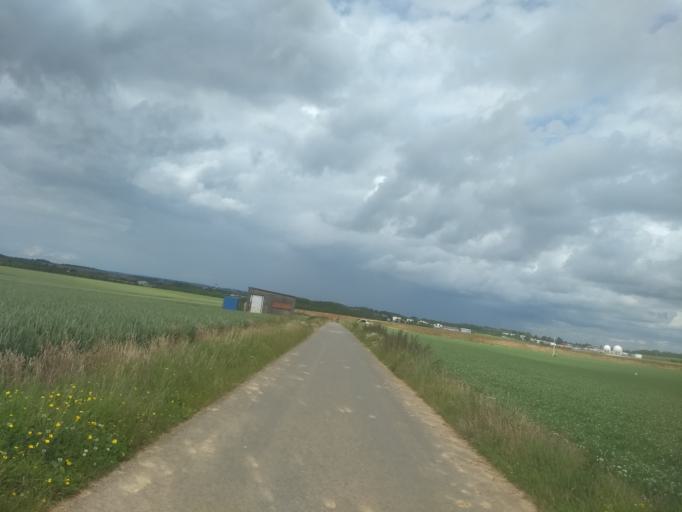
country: FR
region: Nord-Pas-de-Calais
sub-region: Departement du Pas-de-Calais
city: Dainville
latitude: 50.2616
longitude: 2.7077
